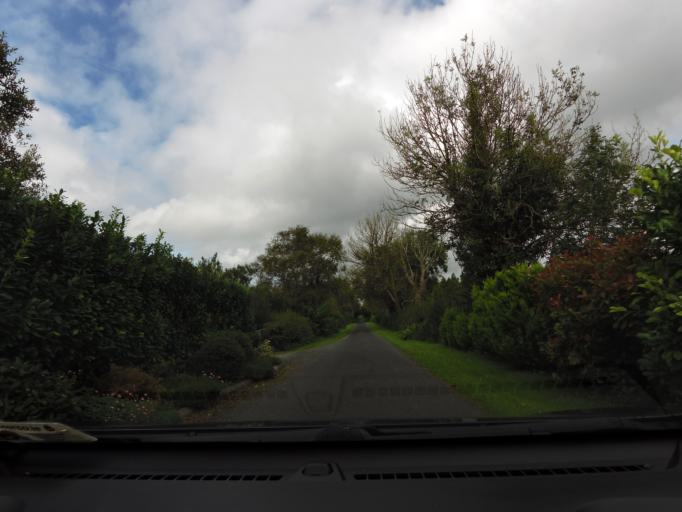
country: IE
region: Connaught
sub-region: County Galway
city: Athenry
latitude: 53.2919
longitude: -8.6634
